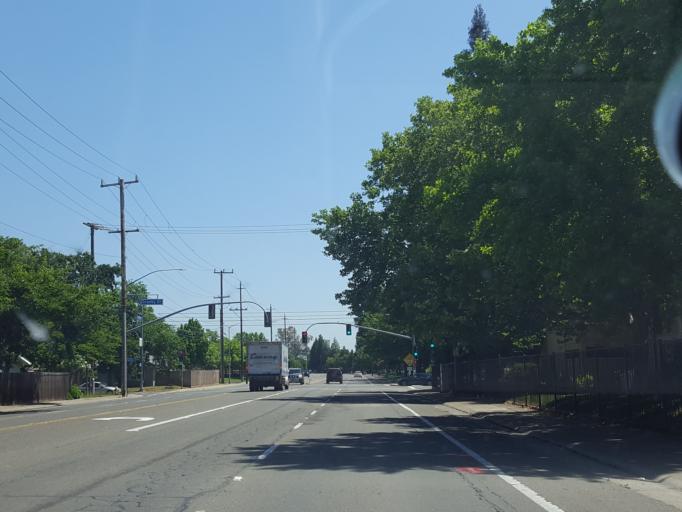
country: US
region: California
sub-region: Sacramento County
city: La Riviera
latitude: 38.5570
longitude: -121.3319
